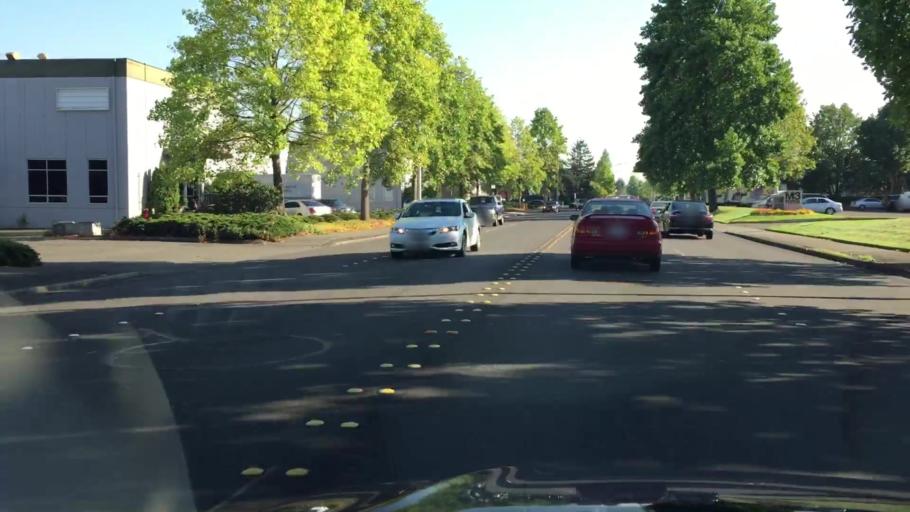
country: US
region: Washington
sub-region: King County
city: Tukwila
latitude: 47.4479
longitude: -122.2508
